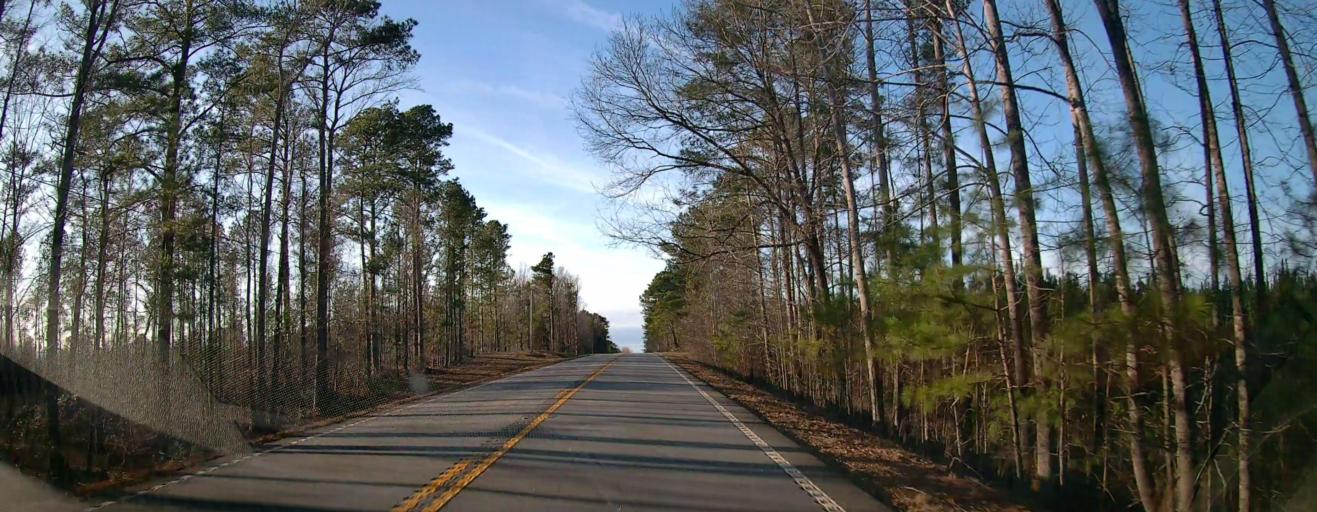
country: US
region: Alabama
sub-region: Chambers County
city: Valley
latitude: 32.7824
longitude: -85.0934
